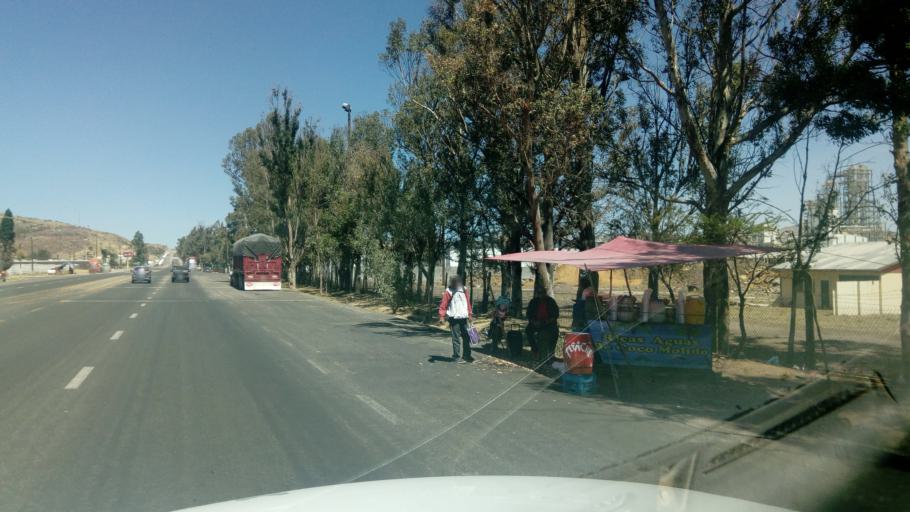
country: MX
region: Durango
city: Victoria de Durango
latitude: 24.0772
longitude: -104.6649
